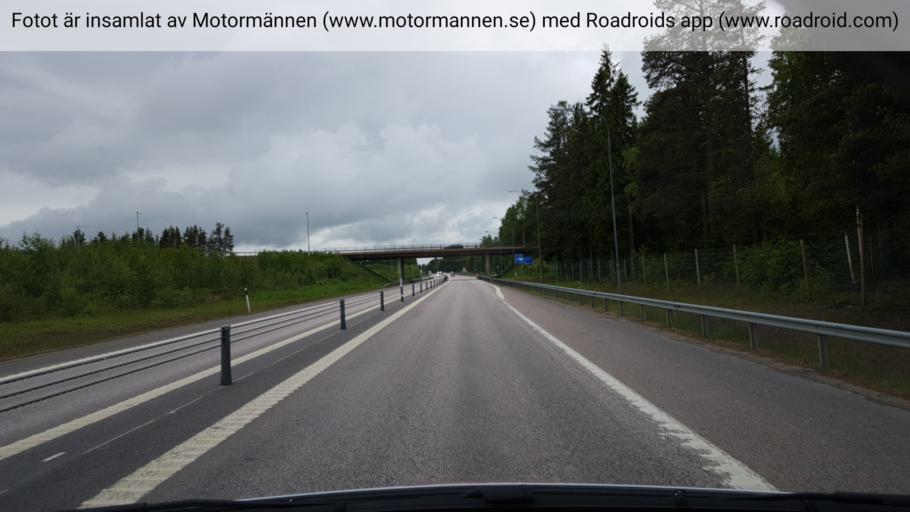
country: SE
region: Vaesterbotten
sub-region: Nordmalings Kommun
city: Nordmaling
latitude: 63.5506
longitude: 19.4156
